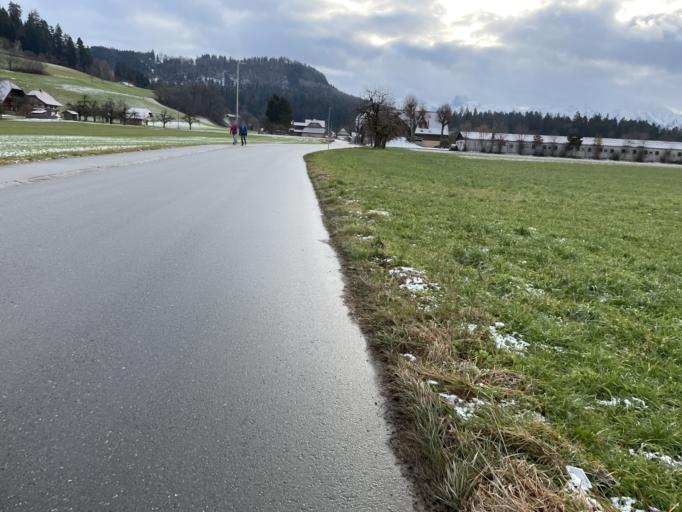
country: CH
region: Bern
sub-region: Thun District
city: Heimberg
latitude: 46.8151
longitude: 7.6140
